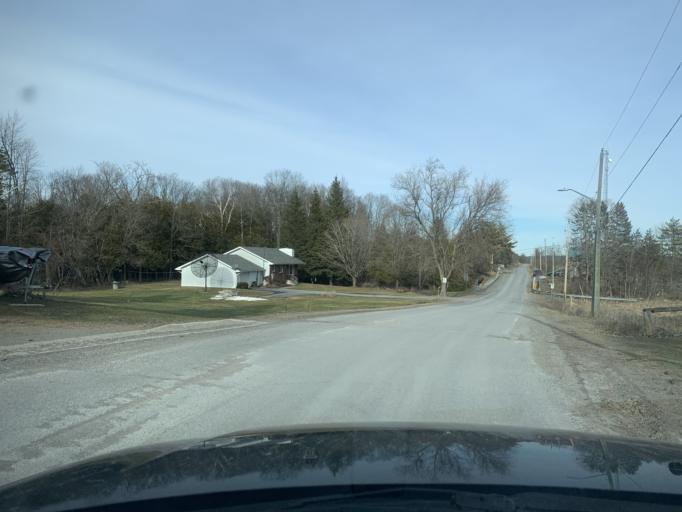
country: CA
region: Ontario
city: Greater Napanee
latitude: 44.4368
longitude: -77.0947
